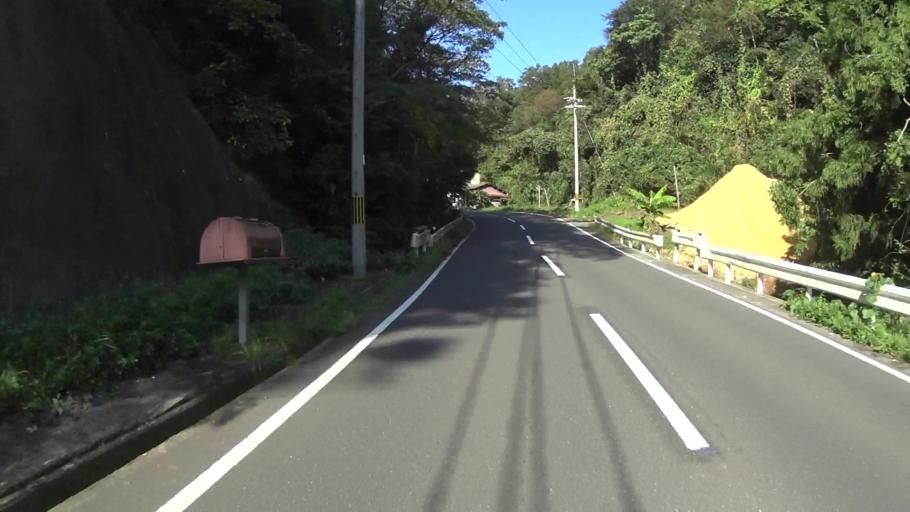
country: JP
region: Kyoto
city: Miyazu
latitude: 35.5923
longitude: 135.1598
